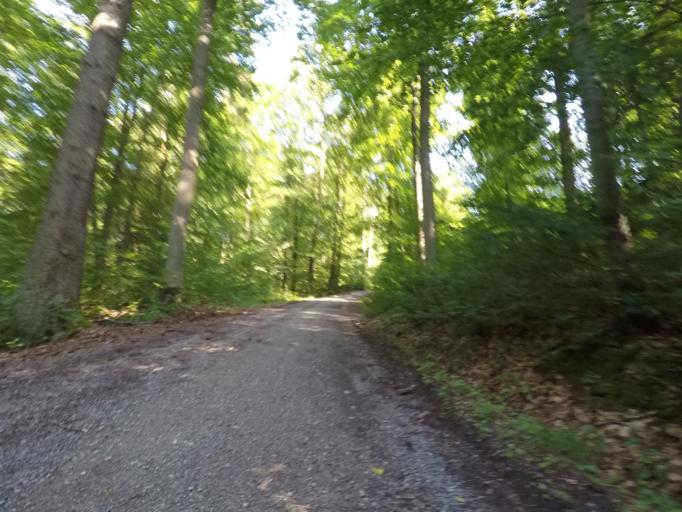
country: DE
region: Baden-Wuerttemberg
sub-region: Regierungsbezirk Stuttgart
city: Ehningen
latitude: 48.6690
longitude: 8.9754
